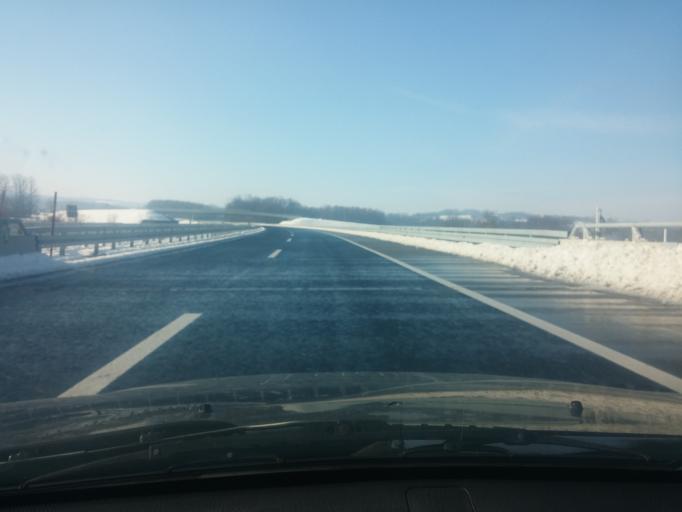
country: BA
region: Republika Srpska
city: Stanari
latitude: 44.8435
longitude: 17.7953
